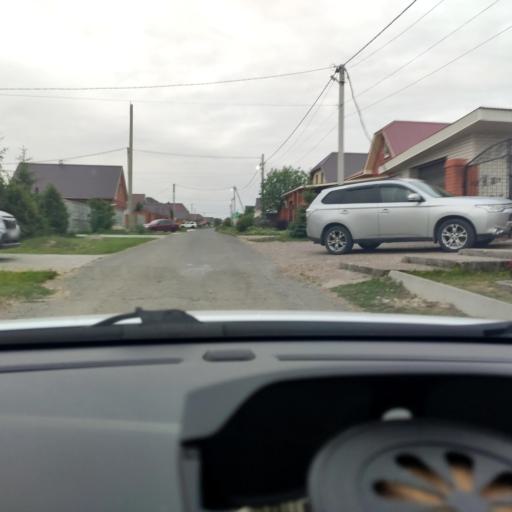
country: RU
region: Tatarstan
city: Vysokaya Gora
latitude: 55.9147
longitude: 49.3345
